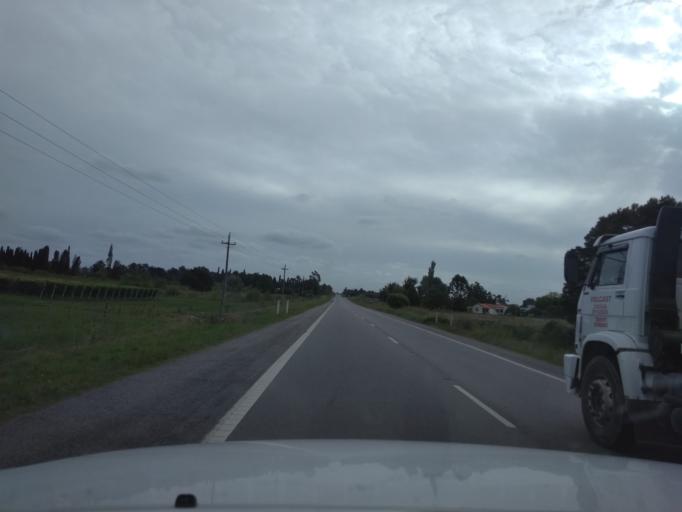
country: UY
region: Canelones
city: Joaquin Suarez
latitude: -34.6838
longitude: -56.0202
